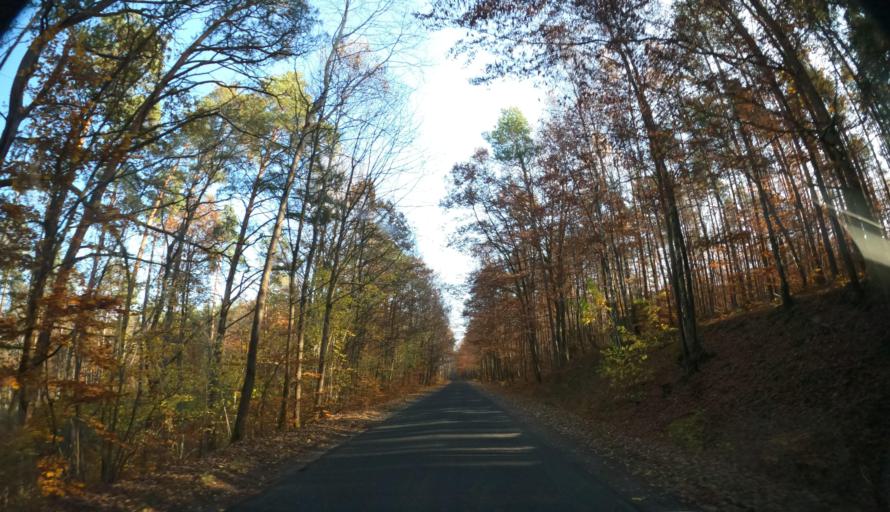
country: PL
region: West Pomeranian Voivodeship
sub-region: Powiat koszalinski
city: Polanow
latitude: 54.2414
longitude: 16.7132
